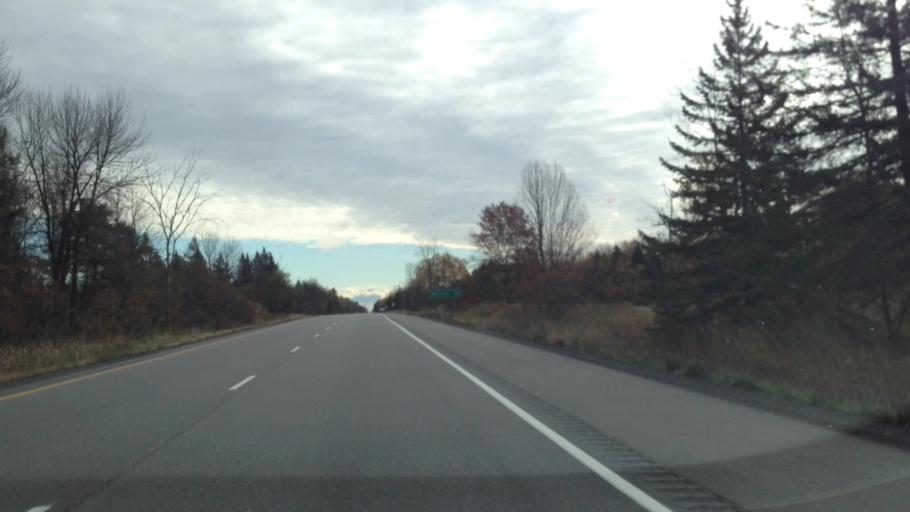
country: CA
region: Ontario
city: Hawkesbury
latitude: 45.5626
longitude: -74.4885
